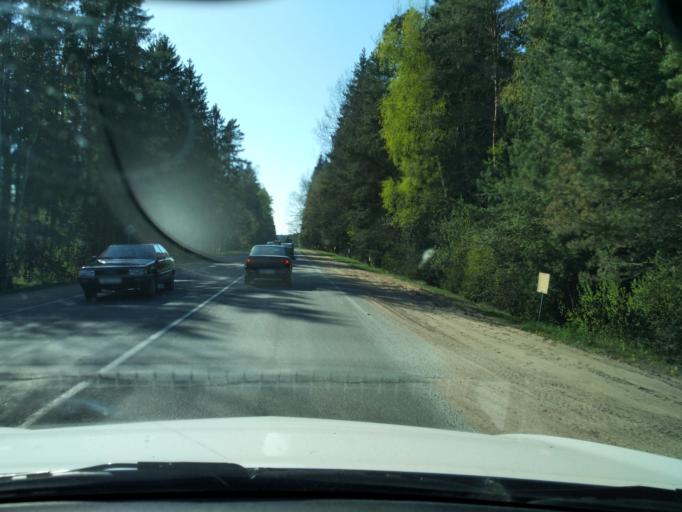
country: BY
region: Minsk
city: Lyeskawka
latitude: 53.9602
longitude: 27.7162
